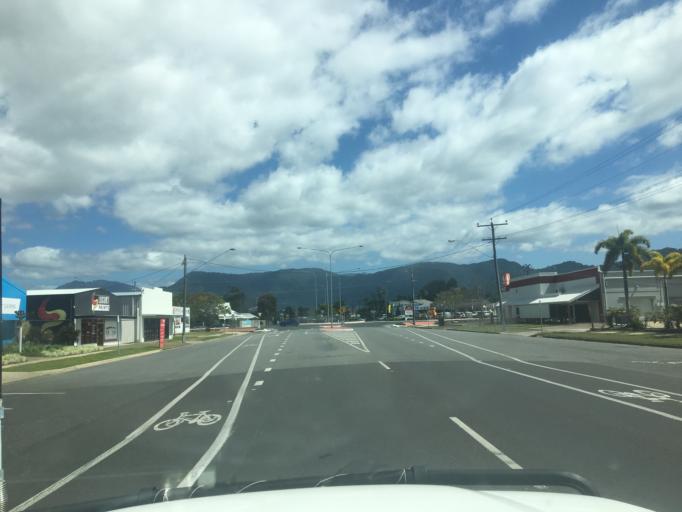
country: AU
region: Queensland
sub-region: Cairns
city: Cairns
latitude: -16.9326
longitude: 145.7619
